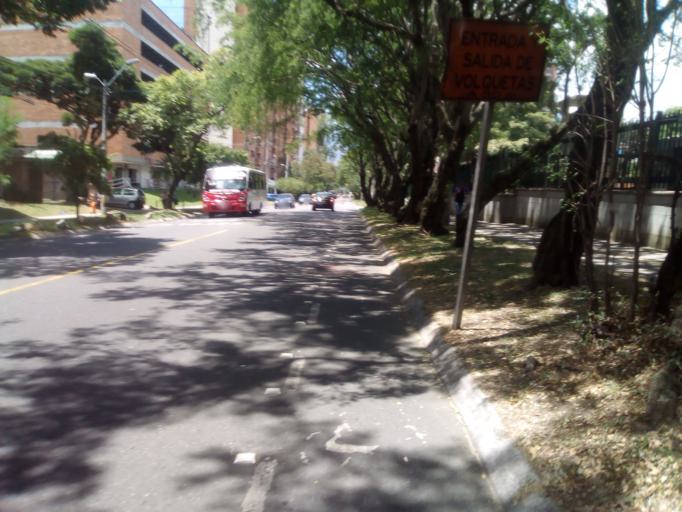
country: CO
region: Antioquia
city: Medellin
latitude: 6.2645
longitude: -75.5913
